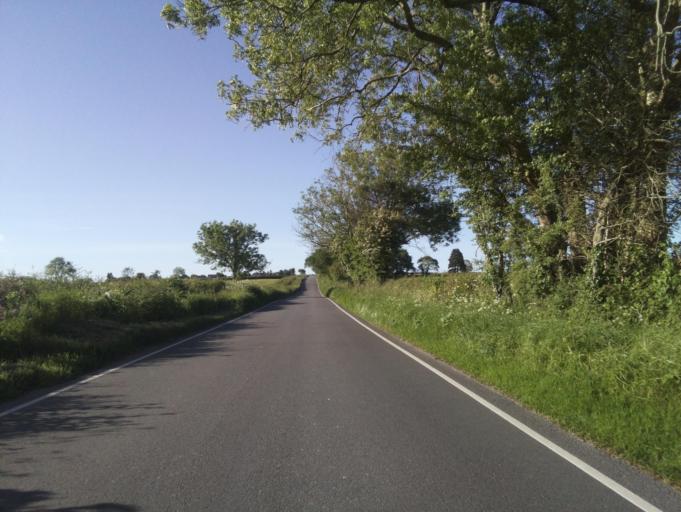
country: GB
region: England
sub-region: Dorset
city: Lyme Regis
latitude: 50.7269
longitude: -2.9901
